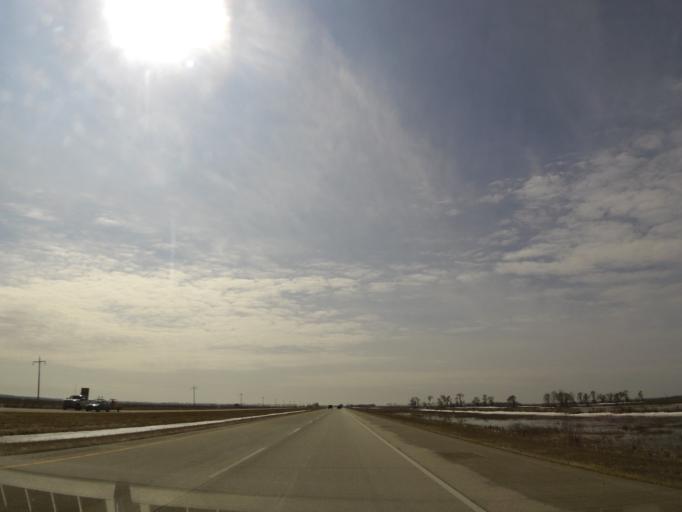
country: US
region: North Dakota
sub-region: Walsh County
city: Grafton
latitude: 48.3804
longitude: -97.1905
